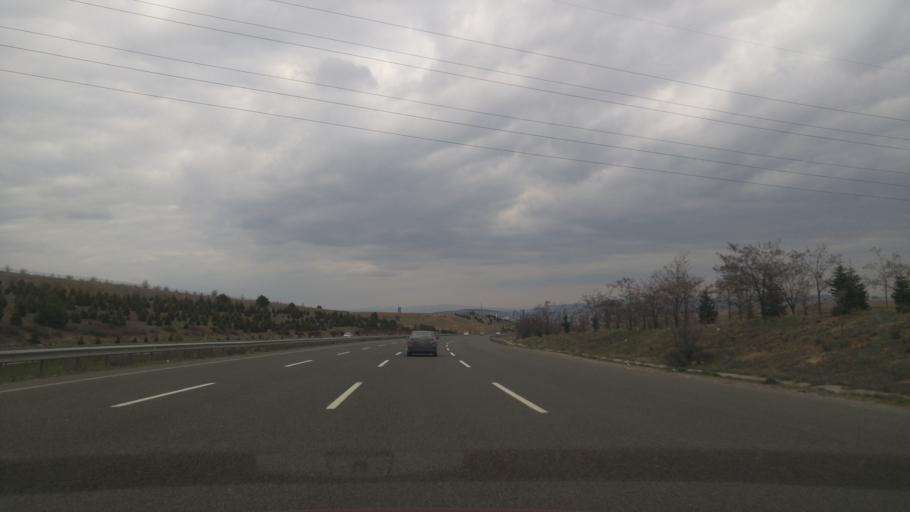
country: TR
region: Ankara
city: Etimesgut
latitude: 39.8062
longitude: 32.6442
